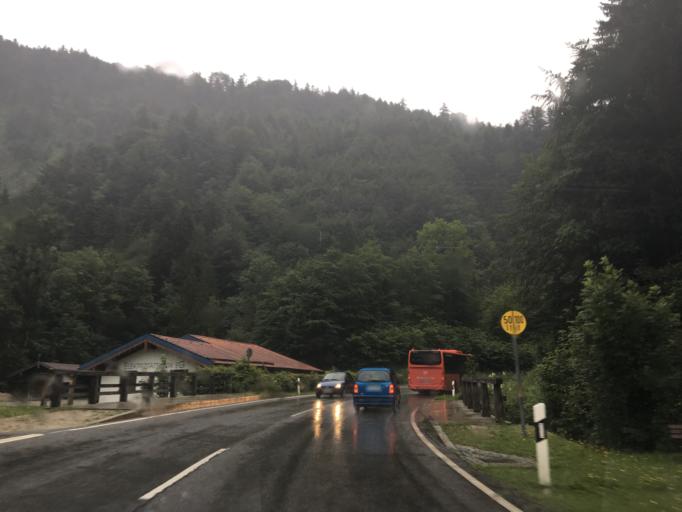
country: DE
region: Bavaria
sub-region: Upper Bavaria
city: Unterwossen
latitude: 47.7063
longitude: 12.4817
